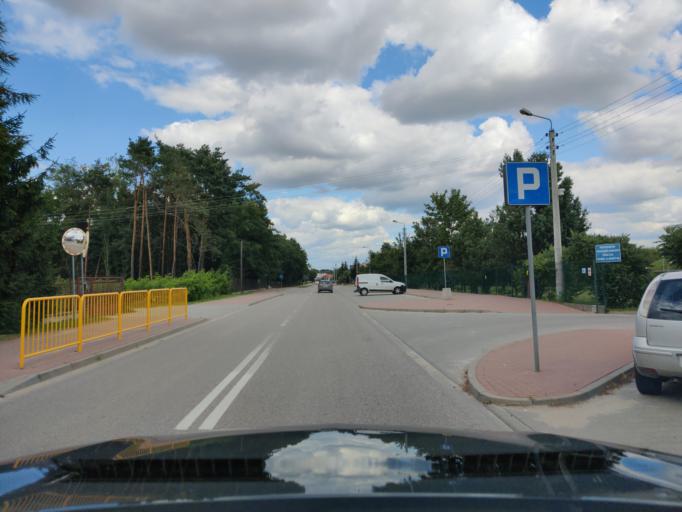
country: PL
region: Masovian Voivodeship
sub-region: Powiat wegrowski
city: Wegrow
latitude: 52.4053
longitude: 22.0251
